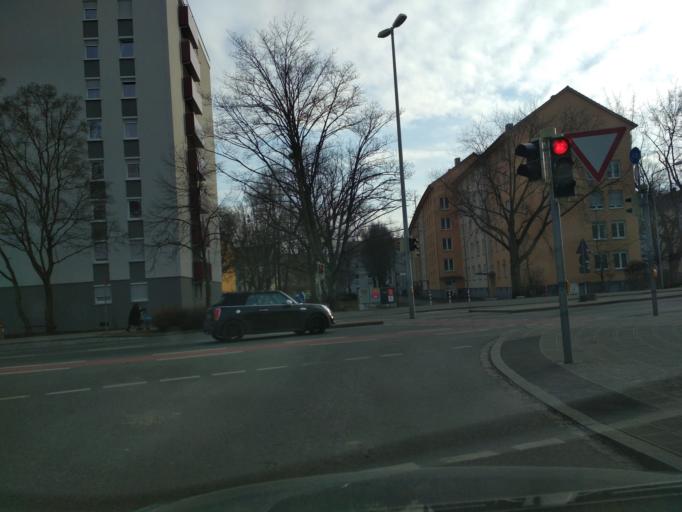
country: DE
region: Bavaria
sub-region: Regierungsbezirk Mittelfranken
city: Grossreuth bei Schweinau
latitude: 49.4424
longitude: 11.0452
